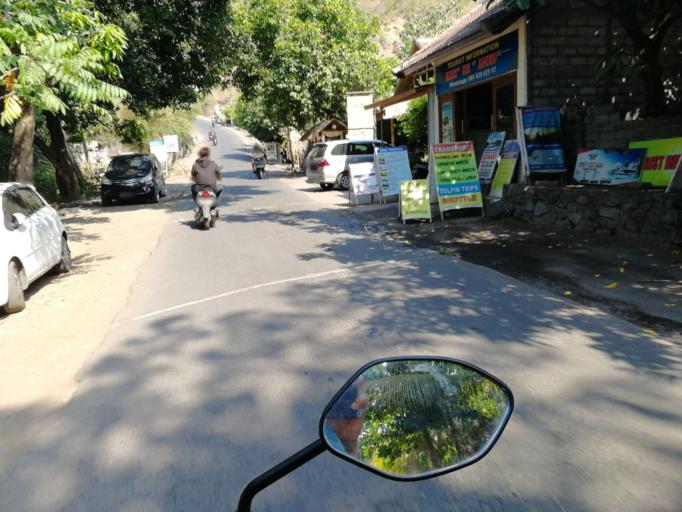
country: ID
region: Bali
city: Biaslantang Kaler
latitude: -8.3391
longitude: 115.6599
